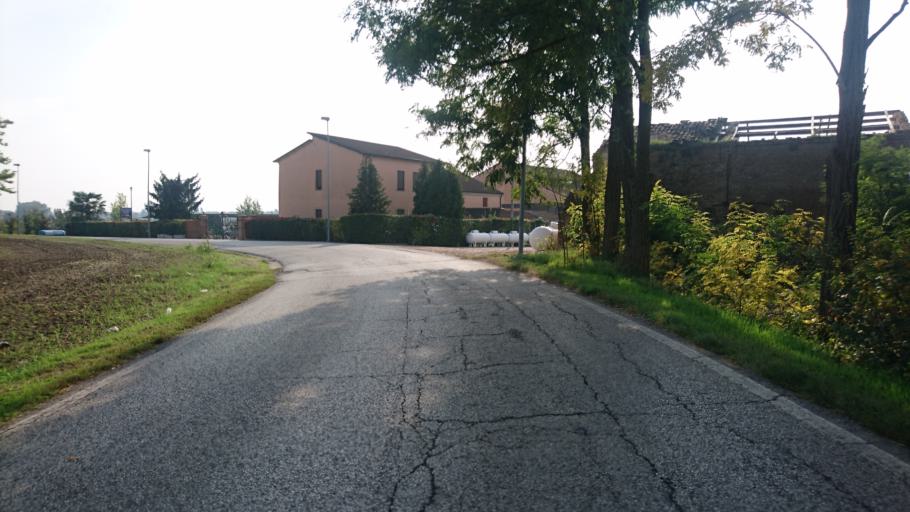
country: IT
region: Veneto
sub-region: Provincia di Rovigo
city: Rovigo
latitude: 45.0530
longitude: 11.7748
